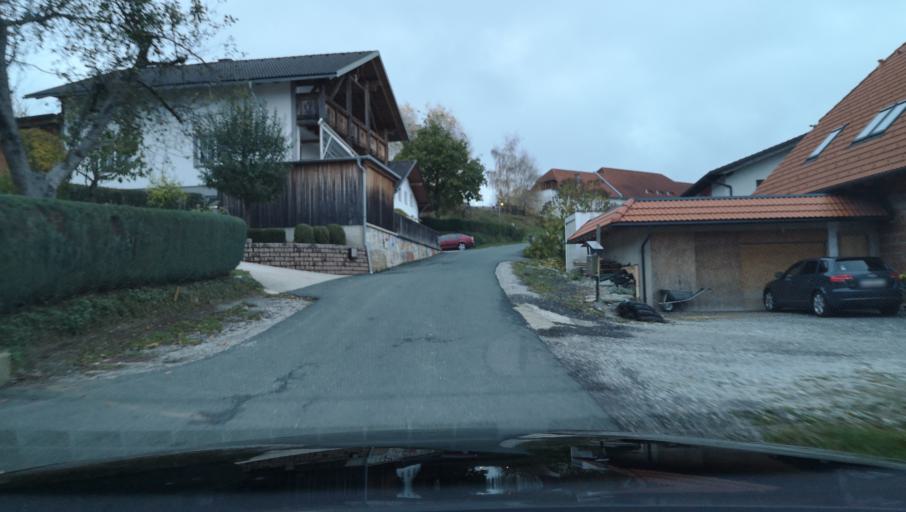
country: AT
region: Styria
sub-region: Politischer Bezirk Weiz
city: Birkfeld
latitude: 47.3489
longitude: 15.6881
